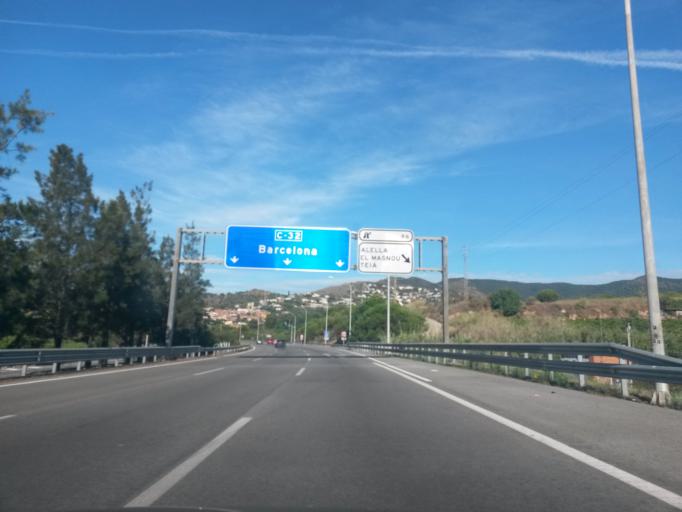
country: ES
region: Catalonia
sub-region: Provincia de Barcelona
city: Alella
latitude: 41.4893
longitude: 2.3063
